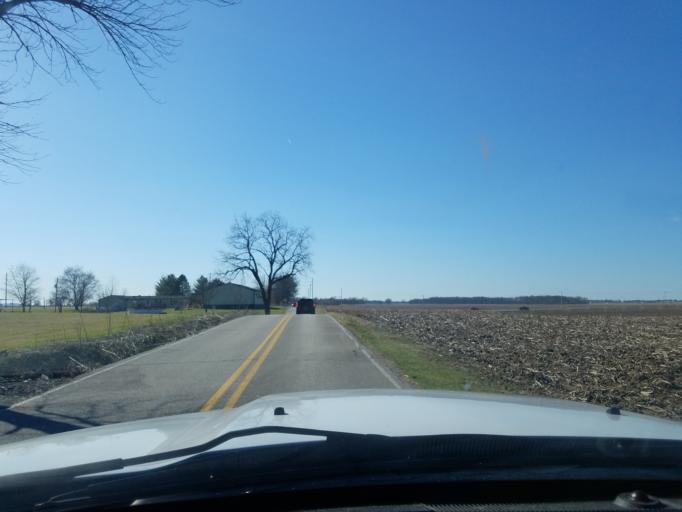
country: US
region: Indiana
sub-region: Johnson County
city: Franklin
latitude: 39.4955
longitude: -85.9678
